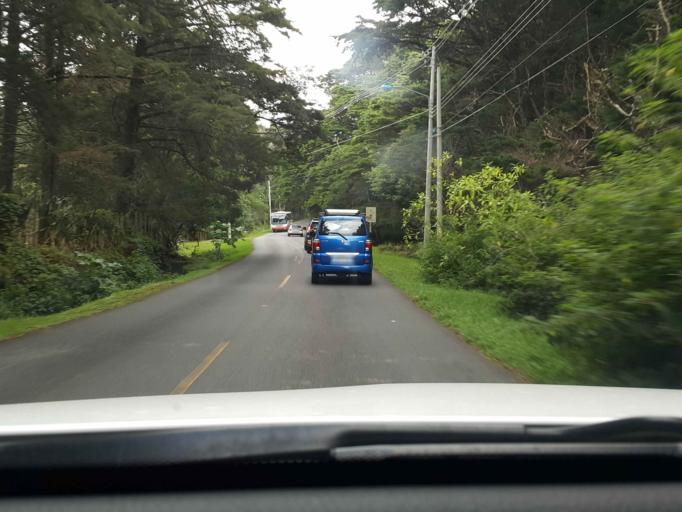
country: CR
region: Heredia
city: San Josecito
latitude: 10.0586
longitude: -84.0857
